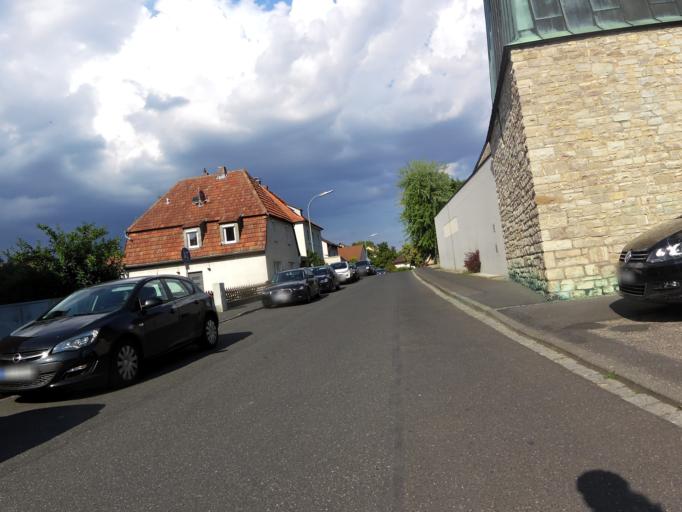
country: DE
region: Bavaria
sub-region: Regierungsbezirk Unterfranken
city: Wuerzburg
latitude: 49.8226
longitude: 9.9620
